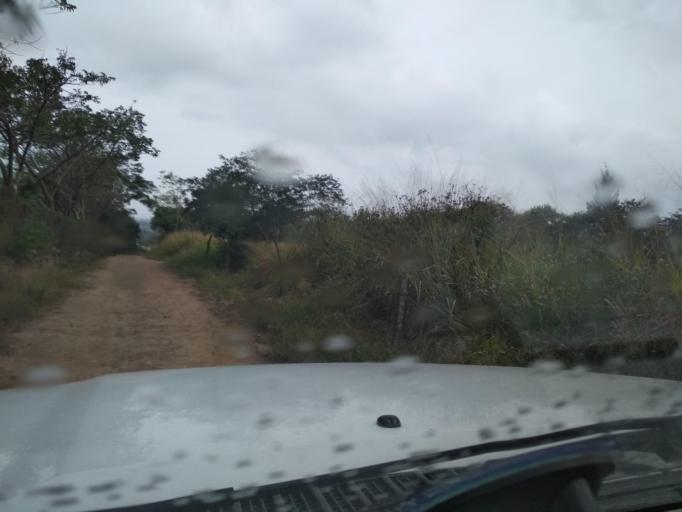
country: MX
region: Veracruz
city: El Castillo
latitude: 19.5373
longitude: -96.8275
